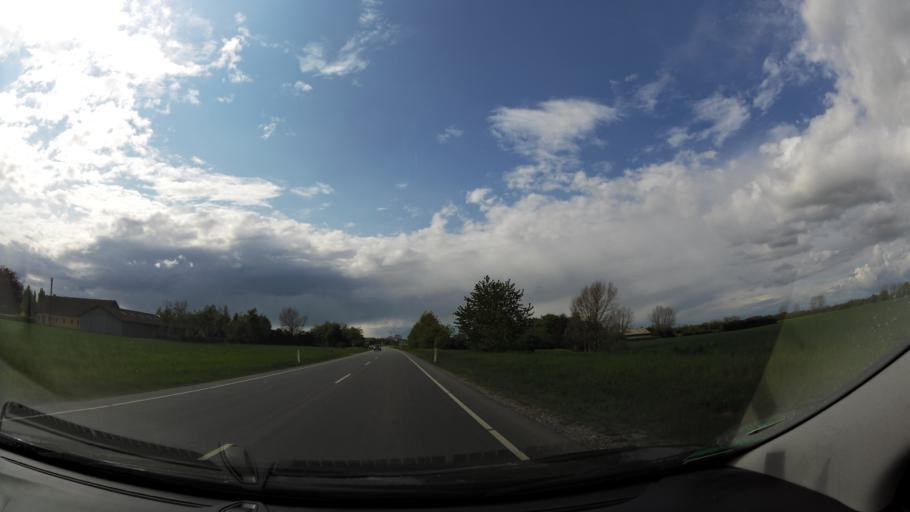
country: DK
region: South Denmark
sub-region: Nyborg Kommune
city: Nyborg
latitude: 55.3200
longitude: 10.7400
